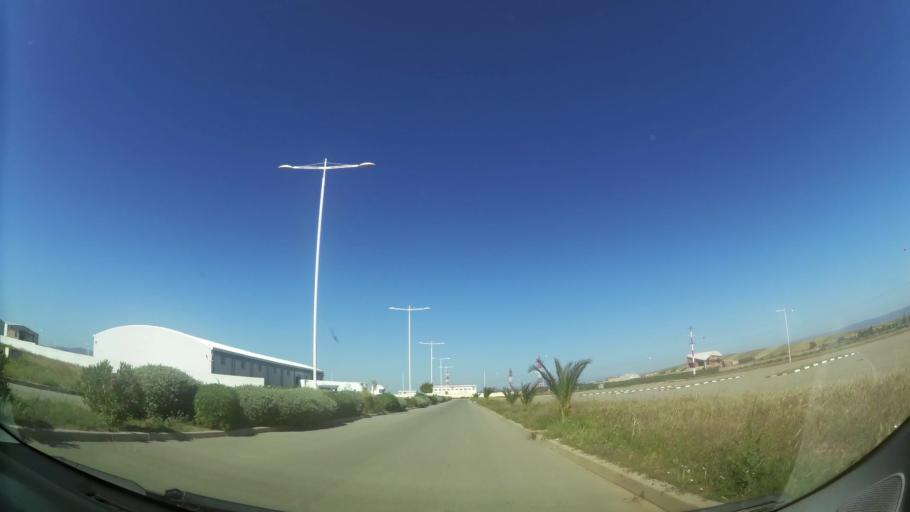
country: MA
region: Oriental
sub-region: Oujda-Angad
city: Oujda
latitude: 34.7695
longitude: -1.9304
